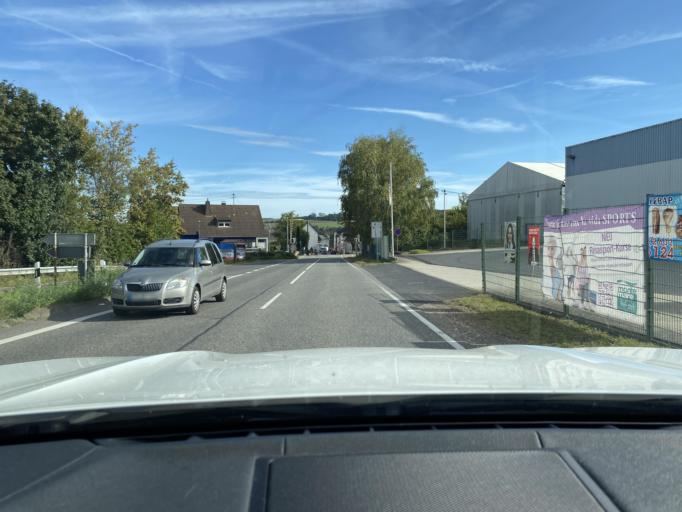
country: DE
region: Rheinland-Pfalz
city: Plaidt
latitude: 50.4045
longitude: 7.4067
